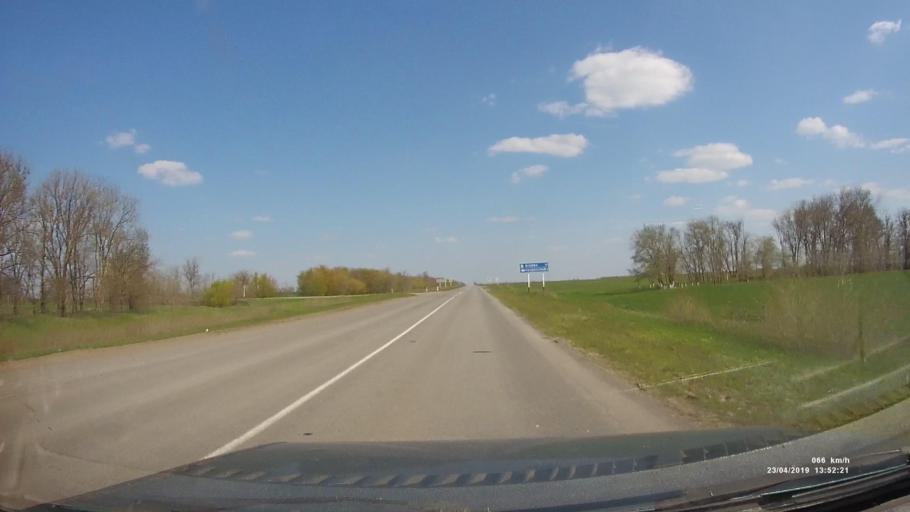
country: RU
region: Rostov
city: Remontnoye
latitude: 46.5995
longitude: 42.9518
